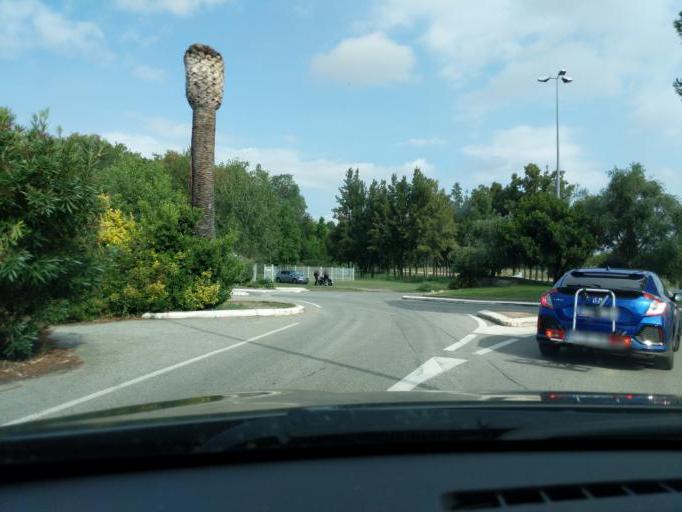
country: FR
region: Corsica
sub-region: Departement de la Haute-Corse
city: Ghisonaccia
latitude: 42.0038
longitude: 9.4413
